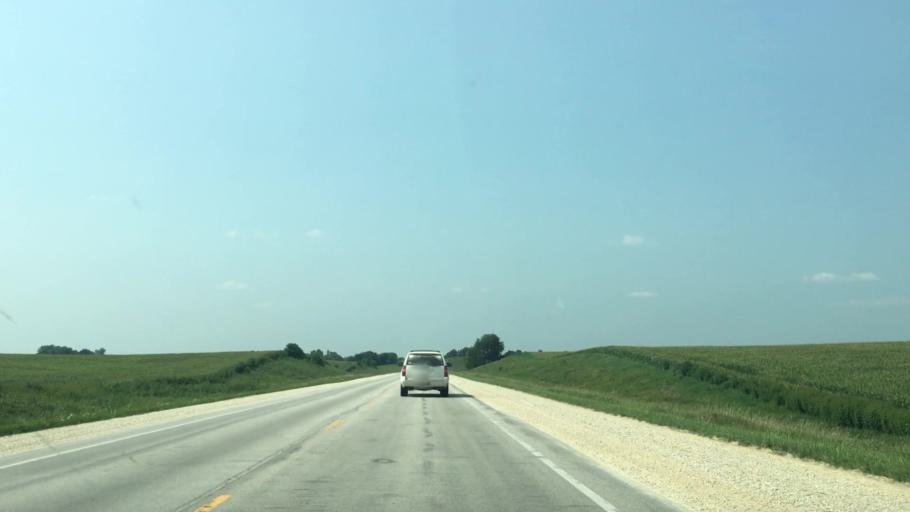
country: US
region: Iowa
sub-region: Winneshiek County
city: Decorah
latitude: 43.3727
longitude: -91.8117
